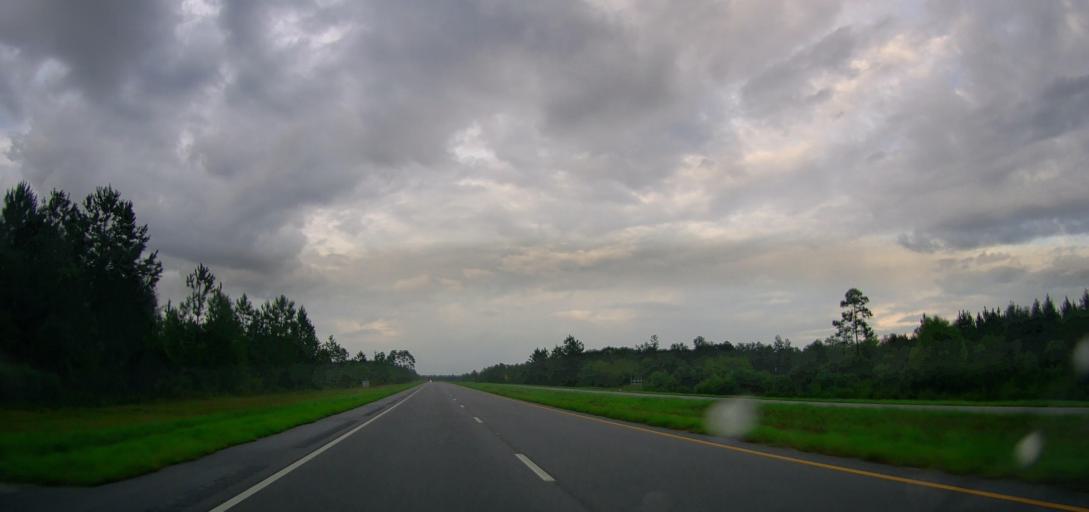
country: US
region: Georgia
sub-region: Ware County
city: Deenwood
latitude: 31.1539
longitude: -82.4378
